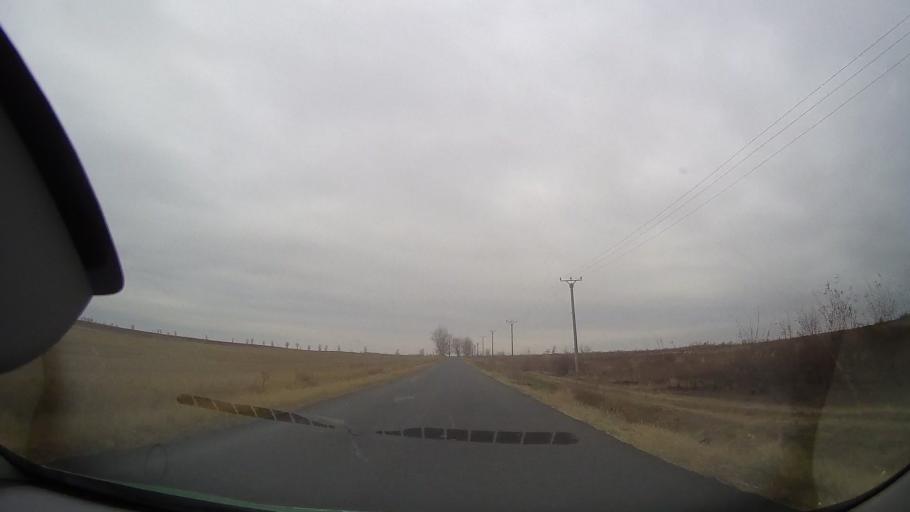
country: RO
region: Braila
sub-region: Comuna Ciresu
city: Ciresu
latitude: 44.9409
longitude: 27.3525
